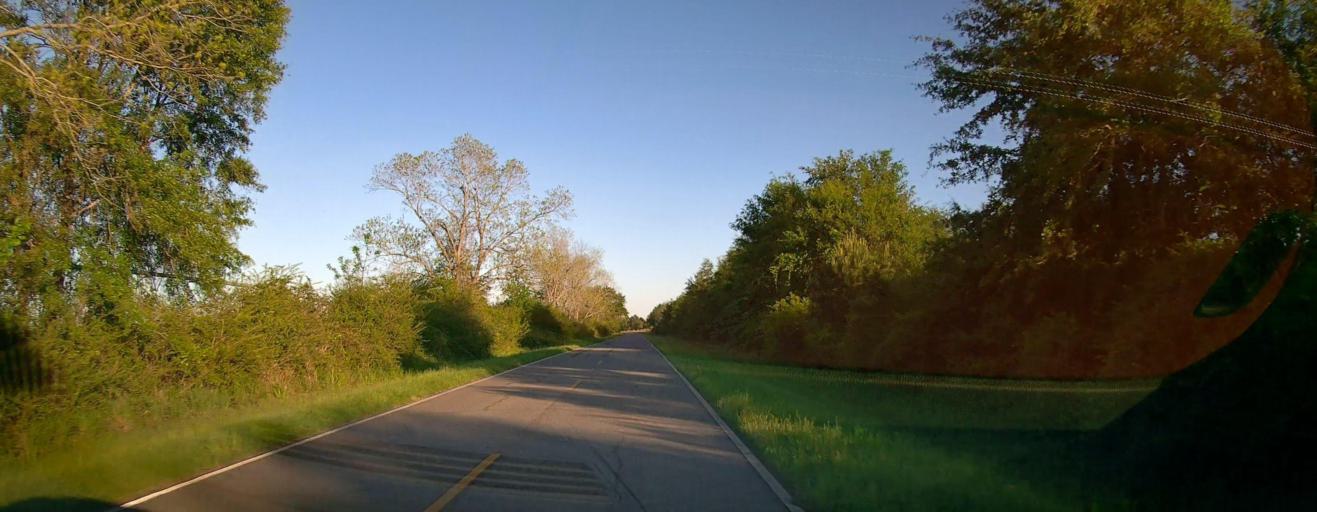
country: US
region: Georgia
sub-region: Ben Hill County
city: Fitzgerald
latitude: 31.6835
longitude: -83.2267
